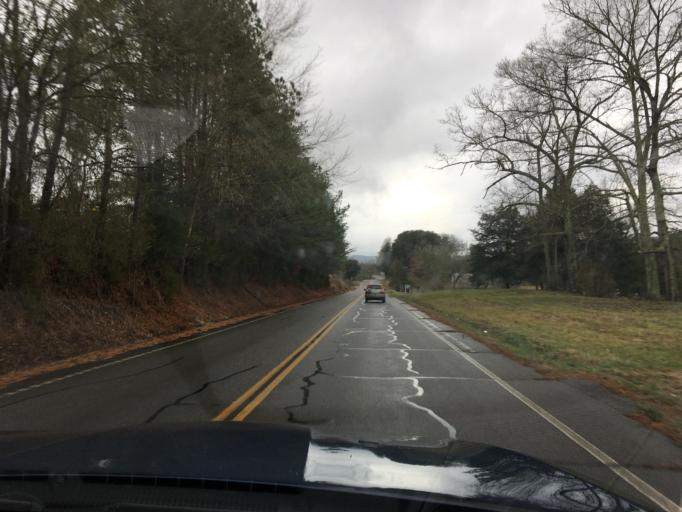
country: US
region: Tennessee
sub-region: Polk County
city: Benton
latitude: 35.1175
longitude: -84.6523
